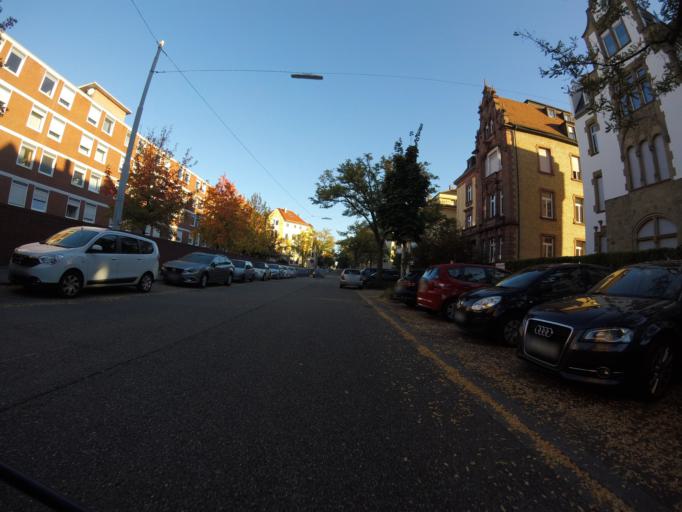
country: DE
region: Baden-Wuerttemberg
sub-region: Karlsruhe Region
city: Karlsruhe
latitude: 48.9991
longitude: 8.3907
